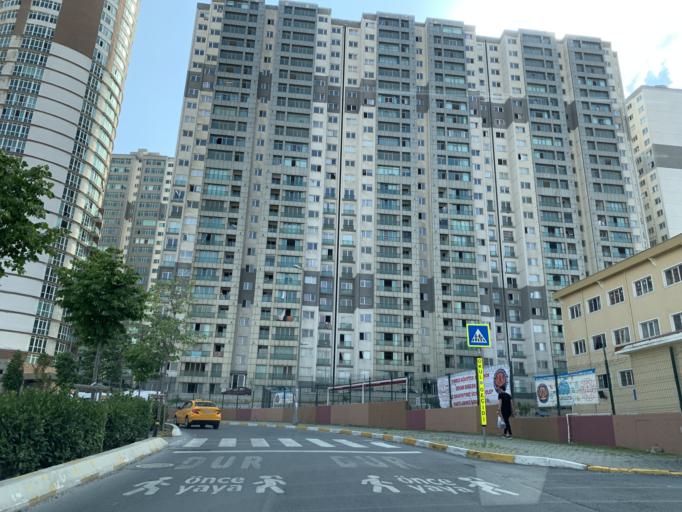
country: TR
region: Istanbul
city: Esenyurt
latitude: 41.0278
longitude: 28.6594
